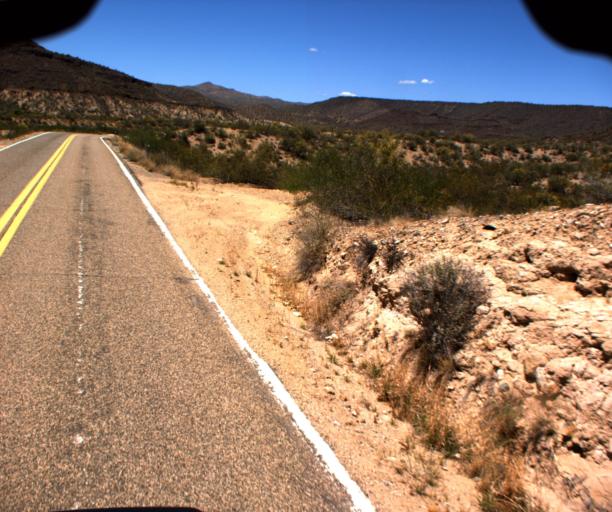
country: US
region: Arizona
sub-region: Yavapai County
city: Bagdad
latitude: 34.4832
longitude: -113.0630
